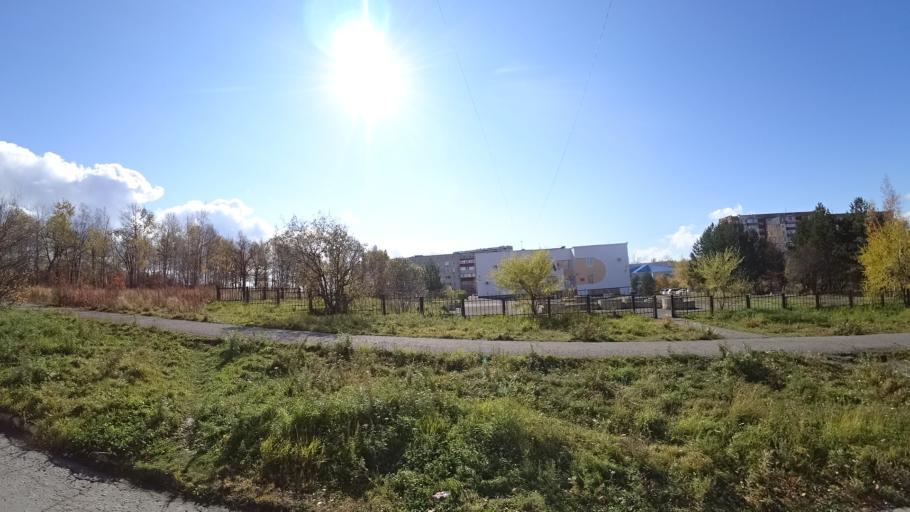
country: RU
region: Khabarovsk Krai
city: Amursk
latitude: 50.2429
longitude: 136.9182
